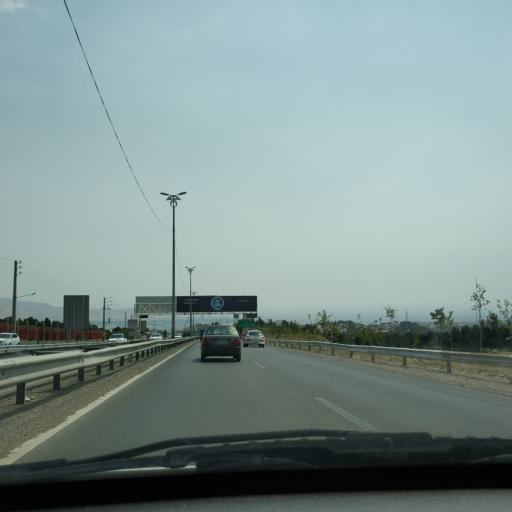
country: IR
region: Tehran
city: Tajrish
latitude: 35.7779
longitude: 51.5615
